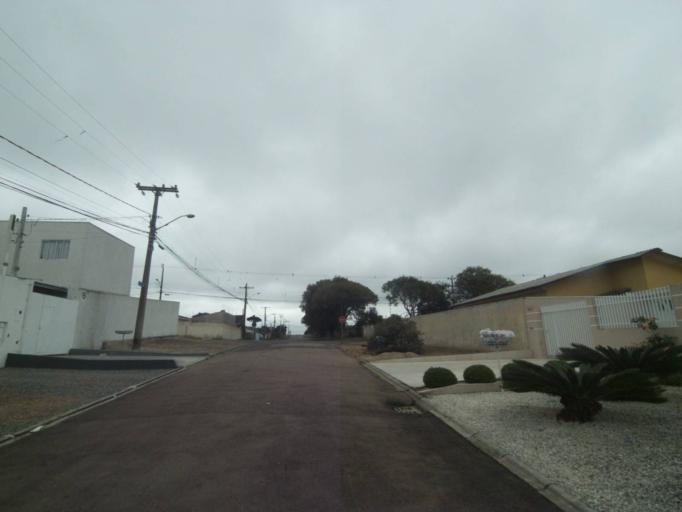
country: BR
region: Parana
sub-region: Sao Jose Dos Pinhais
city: Sao Jose dos Pinhais
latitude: -25.5466
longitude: -49.2845
